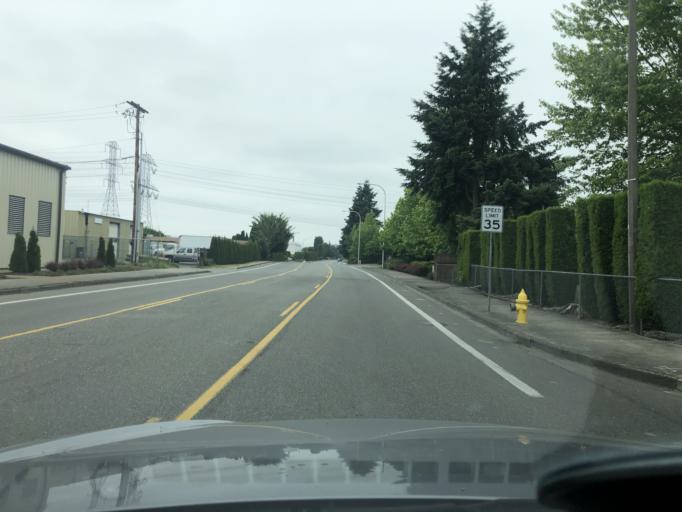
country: US
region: Washington
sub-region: King County
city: Auburn
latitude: 47.3349
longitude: -122.2192
